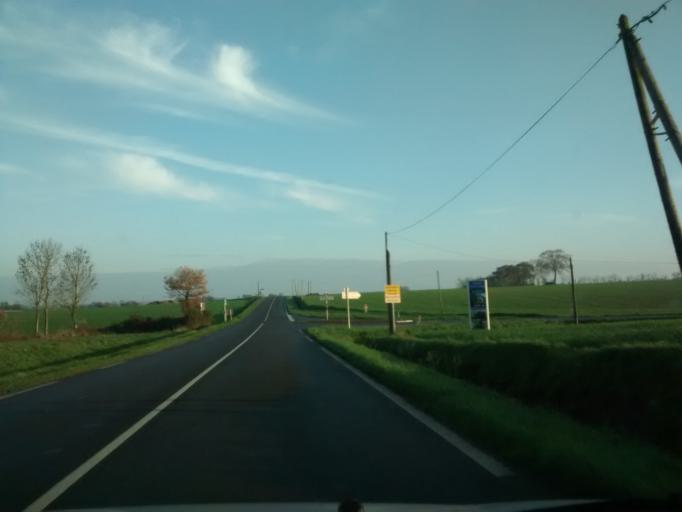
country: FR
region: Brittany
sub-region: Departement d'Ille-et-Vilaine
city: Antrain
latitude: 48.4811
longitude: -1.4713
